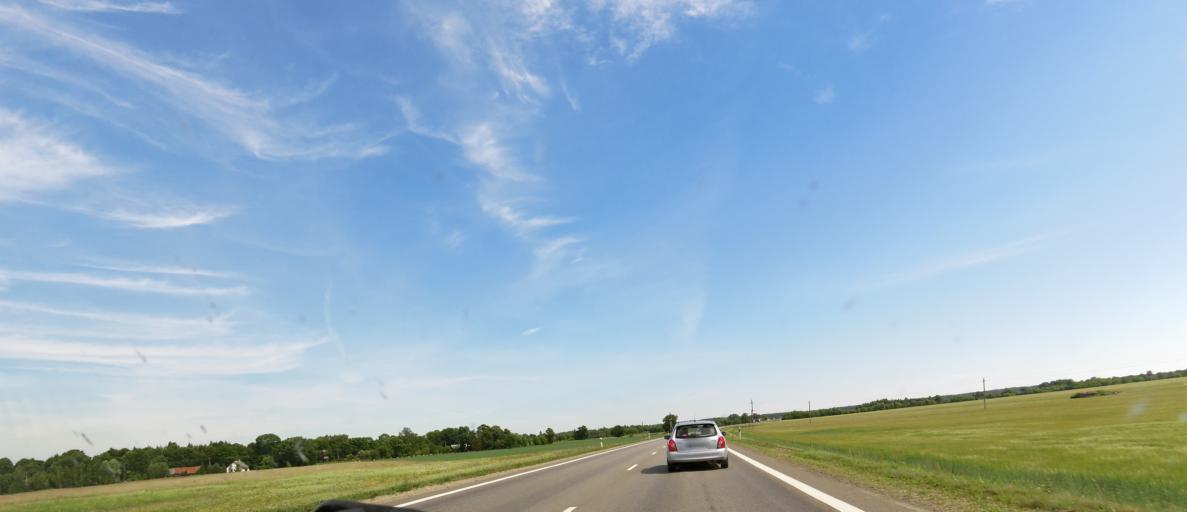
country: LT
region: Panevezys
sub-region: Panevezys City
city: Panevezys
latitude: 55.7927
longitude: 24.3147
